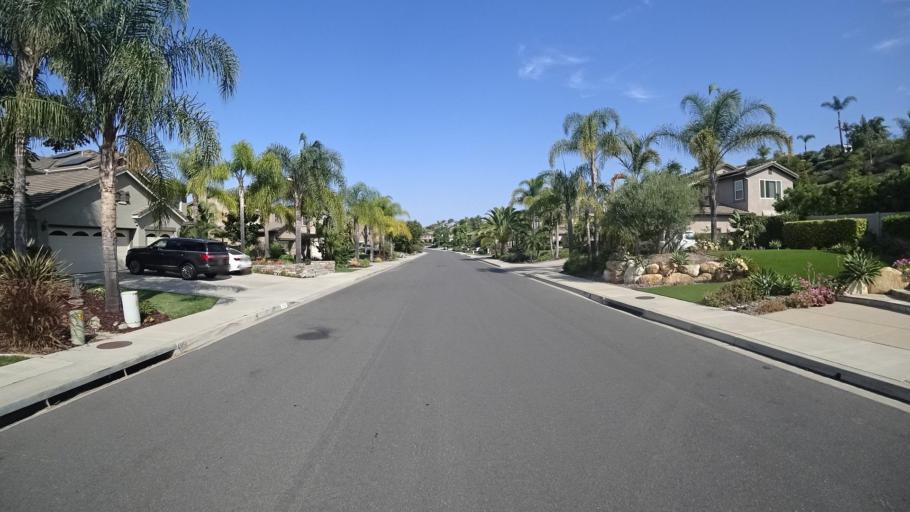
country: US
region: California
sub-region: San Diego County
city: San Marcos
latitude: 33.1616
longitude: -117.1463
